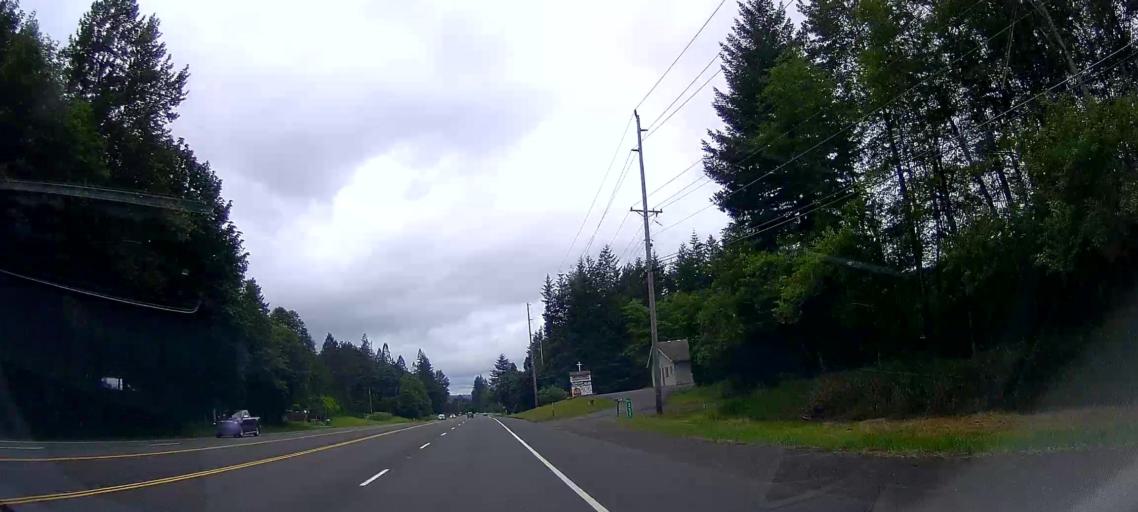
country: US
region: Oregon
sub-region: Clackamas County
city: Mount Hood Village
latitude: 45.3799
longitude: -122.0547
